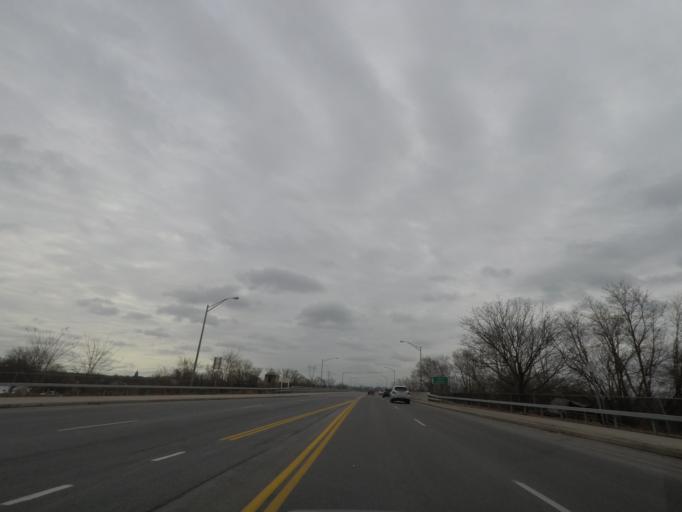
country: US
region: New York
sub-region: Schenectady County
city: Scotia
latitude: 42.8223
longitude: -73.9579
